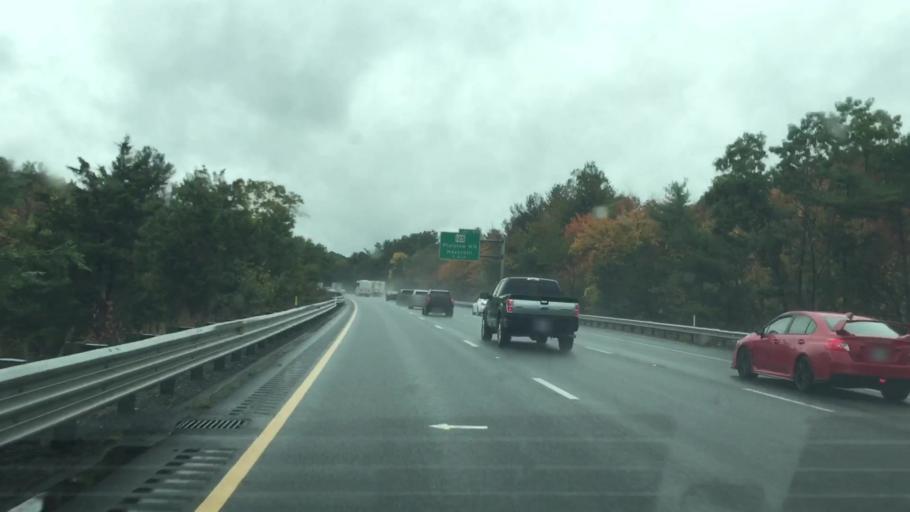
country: US
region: Massachusetts
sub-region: Essex County
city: Haverhill
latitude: 42.8058
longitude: -71.0688
